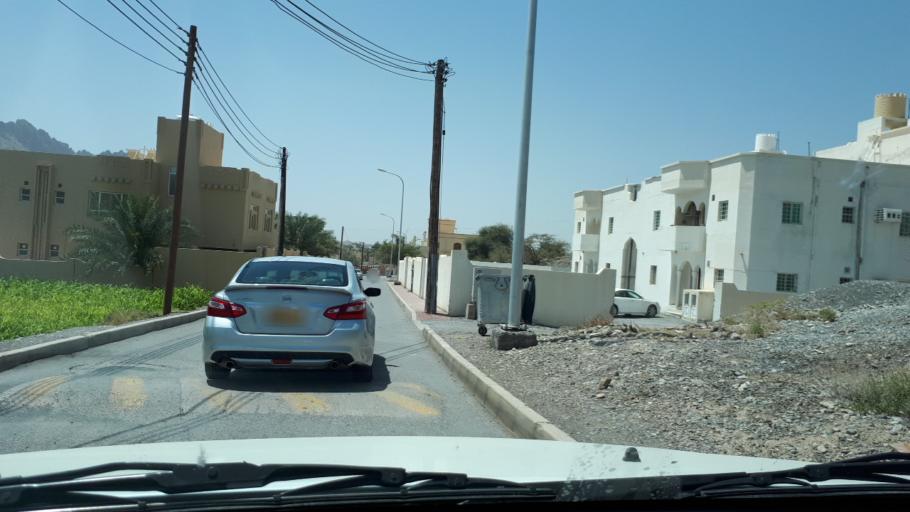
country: OM
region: Muhafazat ad Dakhiliyah
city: Nizwa
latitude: 22.9195
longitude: 57.5301
